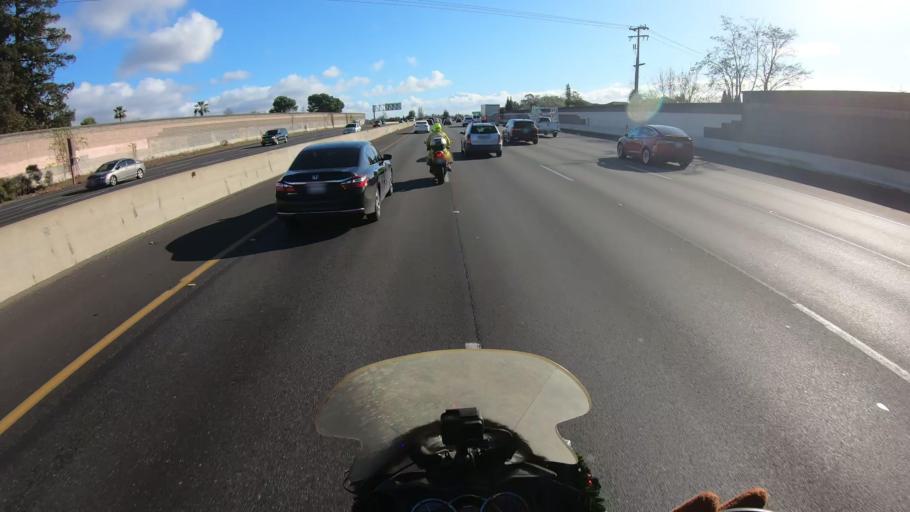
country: US
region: California
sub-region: Alameda County
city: Union City
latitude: 37.5849
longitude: -122.0555
